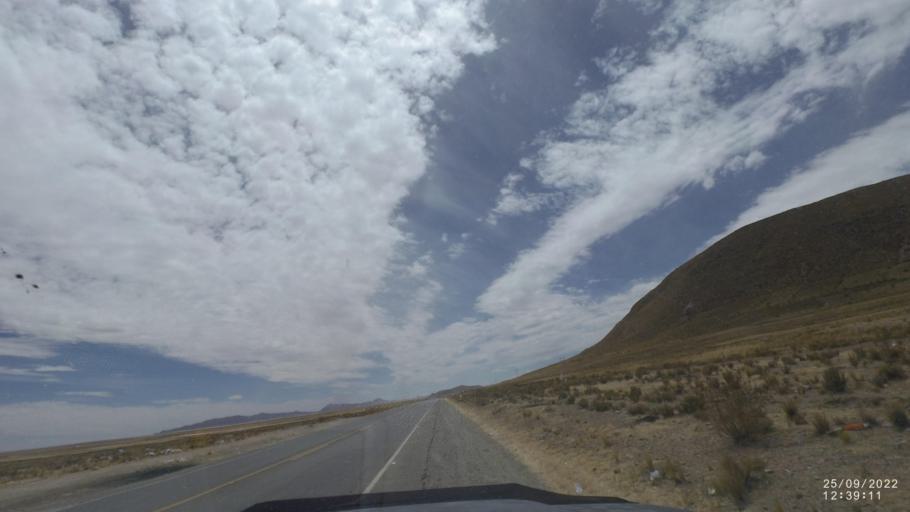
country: BO
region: Oruro
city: Machacamarca
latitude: -18.1251
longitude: -67.0021
